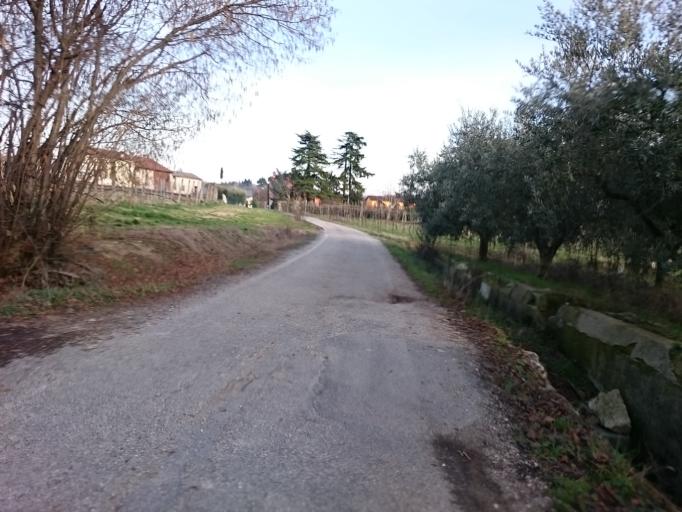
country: IT
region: Veneto
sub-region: Provincia di Verona
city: Cavalcaselle
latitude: 45.4562
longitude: 10.7235
